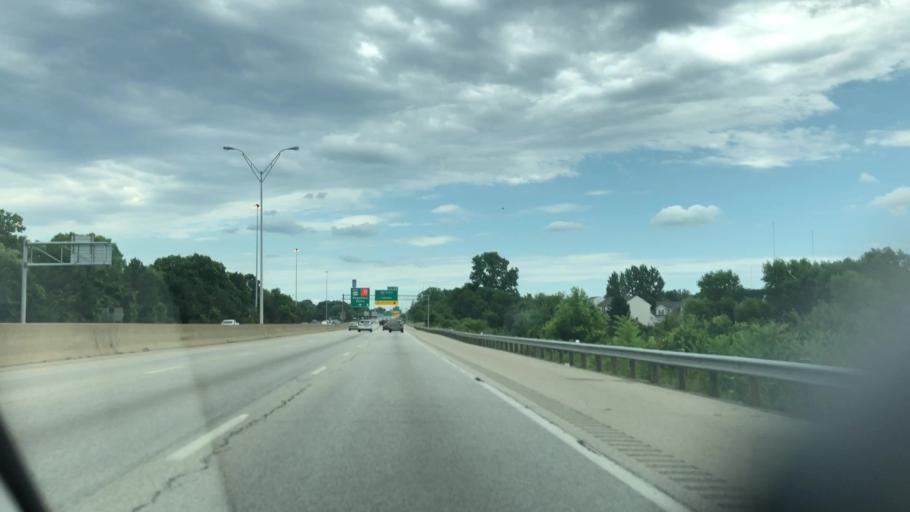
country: US
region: Ohio
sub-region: Summit County
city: Portage Lakes
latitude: 41.0246
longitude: -81.5128
